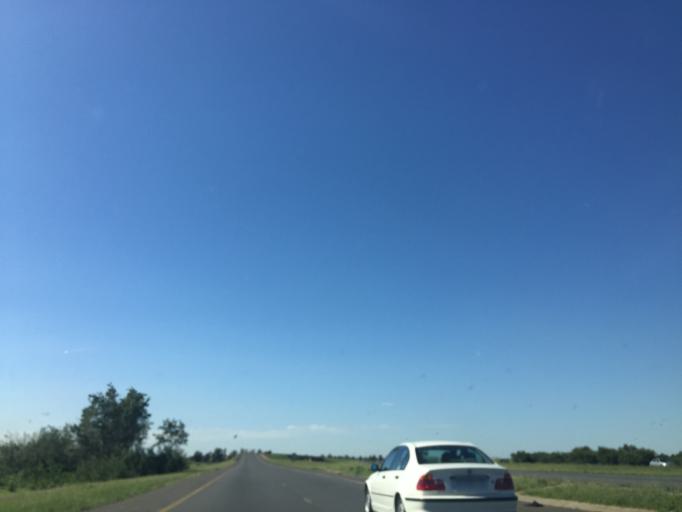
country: ZA
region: Gauteng
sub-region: Sedibeng District Municipality
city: Vereeniging
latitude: -26.6868
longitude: 27.9052
